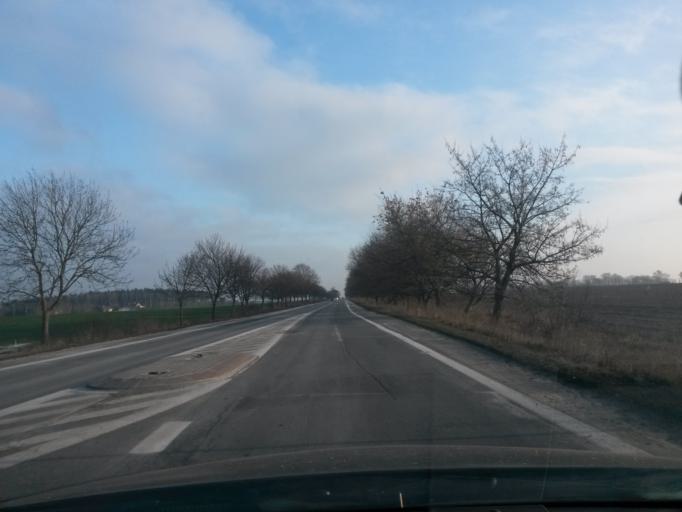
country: PL
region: Greater Poland Voivodeship
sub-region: Powiat poznanski
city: Kobylnica
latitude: 52.4628
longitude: 17.1262
